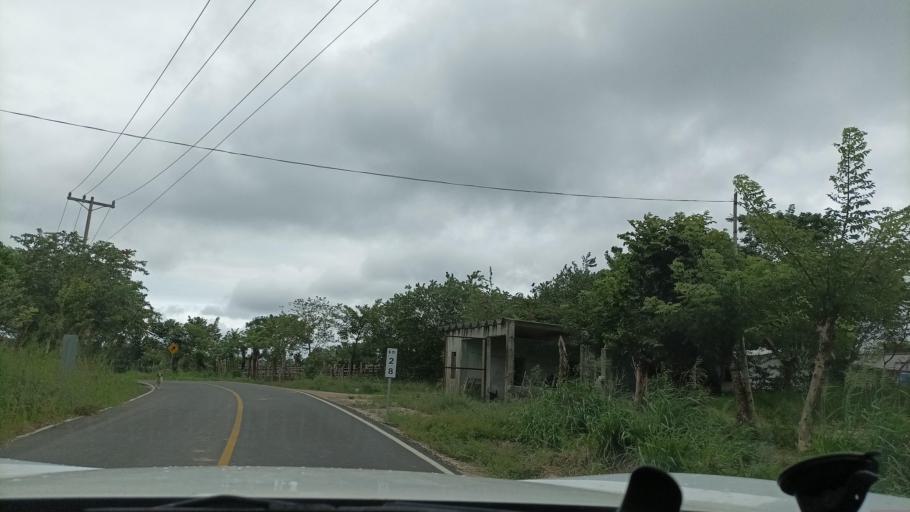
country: MX
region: Veracruz
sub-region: Moloacan
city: Cuichapa
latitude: 17.8089
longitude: -94.3557
